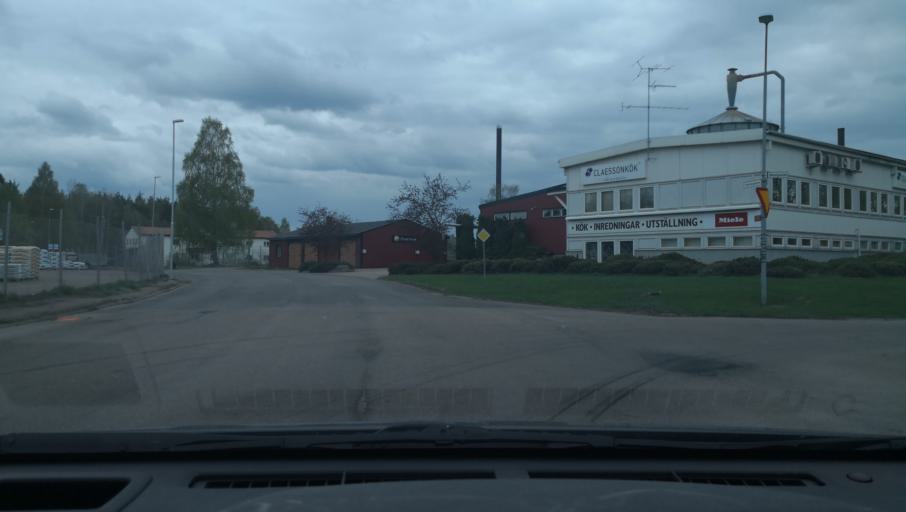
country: SE
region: Dalarna
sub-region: Avesta Kommun
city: Avesta
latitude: 60.1243
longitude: 16.2169
